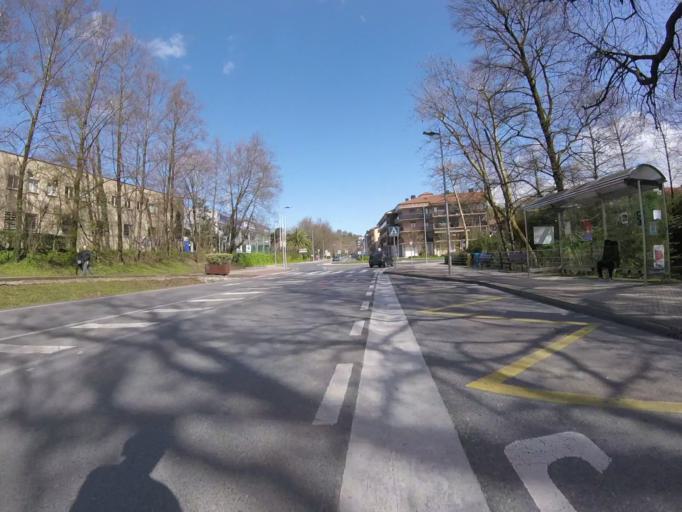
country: ES
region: Basque Country
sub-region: Provincia de Guipuzcoa
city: Astigarraga
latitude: 43.2828
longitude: -1.9499
